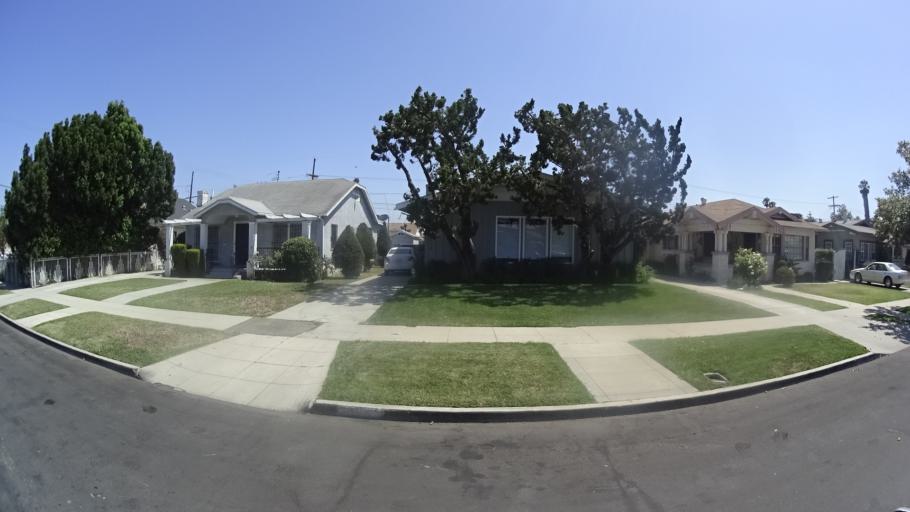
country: US
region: California
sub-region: Los Angeles County
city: View Park-Windsor Hills
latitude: 34.0081
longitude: -118.3142
